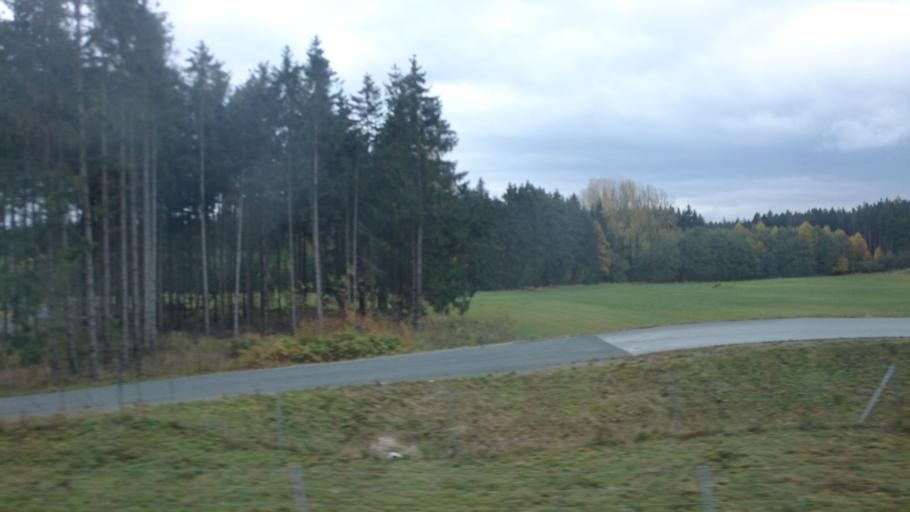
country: DE
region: Thuringia
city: Dittersdorf
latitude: 50.6557
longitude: 11.8148
